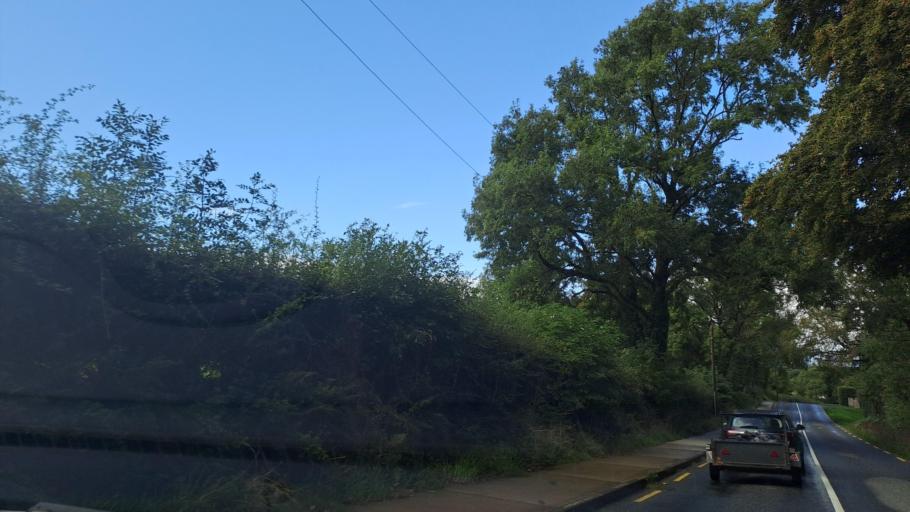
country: IE
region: Ulster
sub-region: An Cabhan
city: Kingscourt
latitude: 53.9163
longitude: -6.8083
